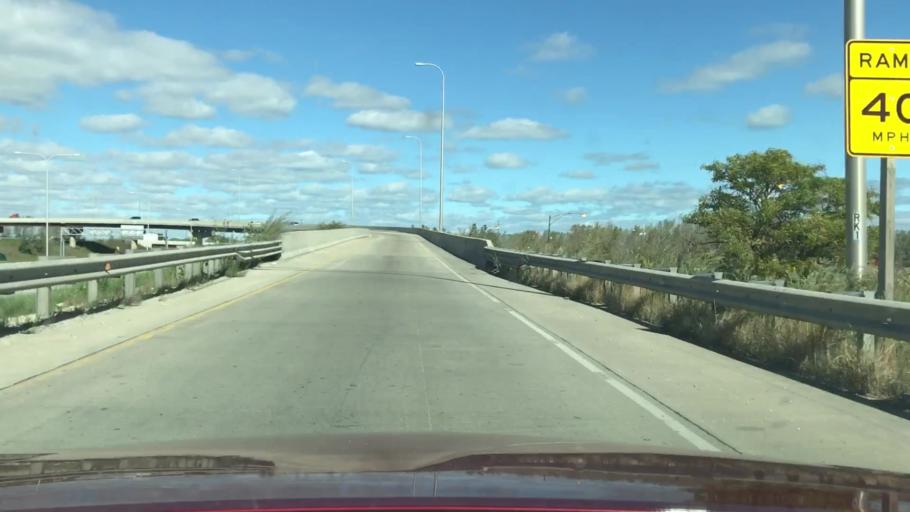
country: US
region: Illinois
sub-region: Cook County
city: Dolton
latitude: 41.7114
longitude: -87.5844
